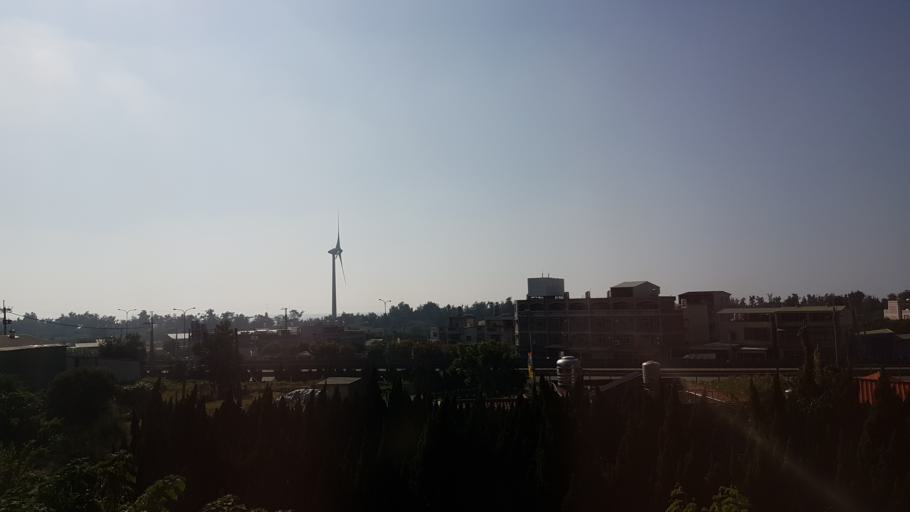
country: TW
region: Taiwan
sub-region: Hsinchu
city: Hsinchu
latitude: 24.7144
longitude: 120.8684
